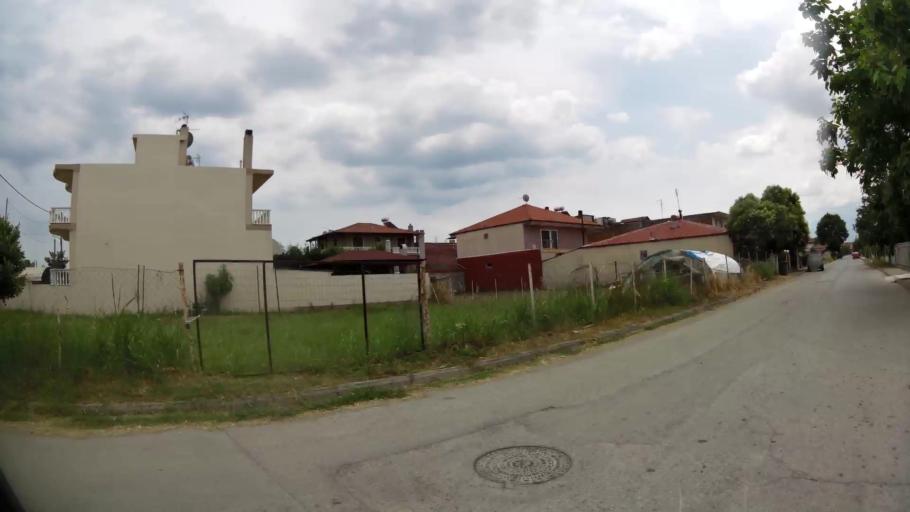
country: GR
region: Central Macedonia
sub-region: Nomos Pierias
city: Kallithea
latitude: 40.2753
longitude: 22.5743
